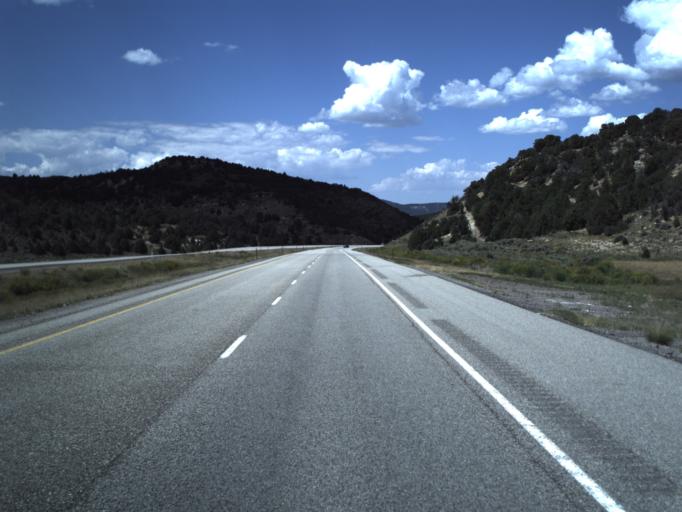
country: US
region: Utah
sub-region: Sevier County
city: Salina
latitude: 38.7867
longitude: -111.4994
